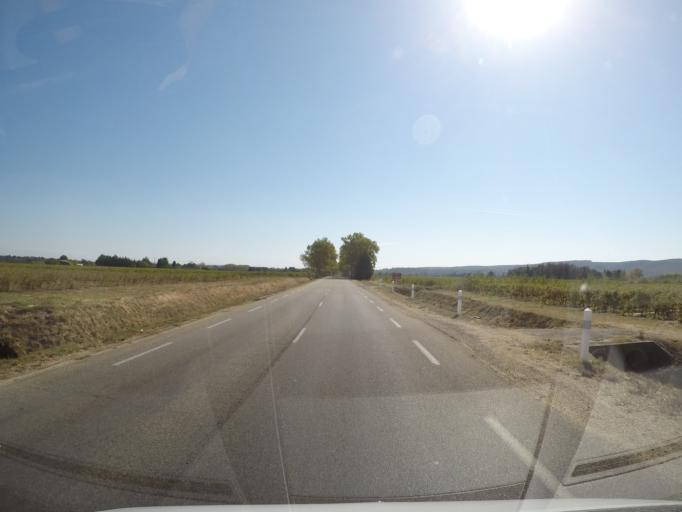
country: FR
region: Languedoc-Roussillon
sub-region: Departement du Gard
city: Castillon-du-Gard
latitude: 43.9694
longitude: 4.5024
